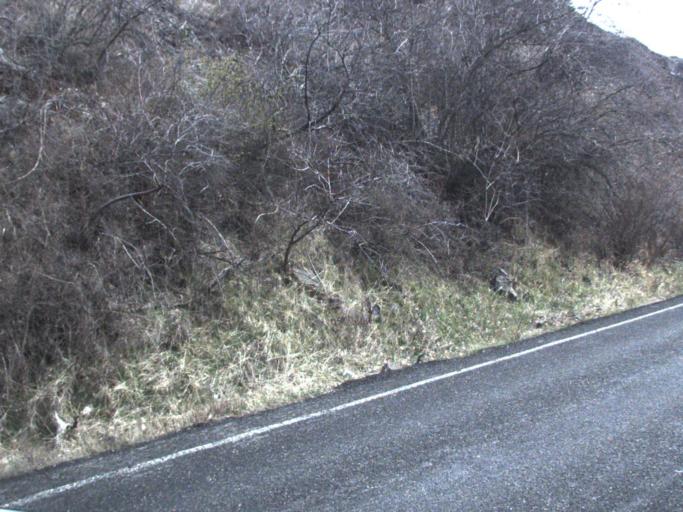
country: US
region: Washington
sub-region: Yakima County
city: Tieton
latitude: 46.8335
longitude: -120.9393
